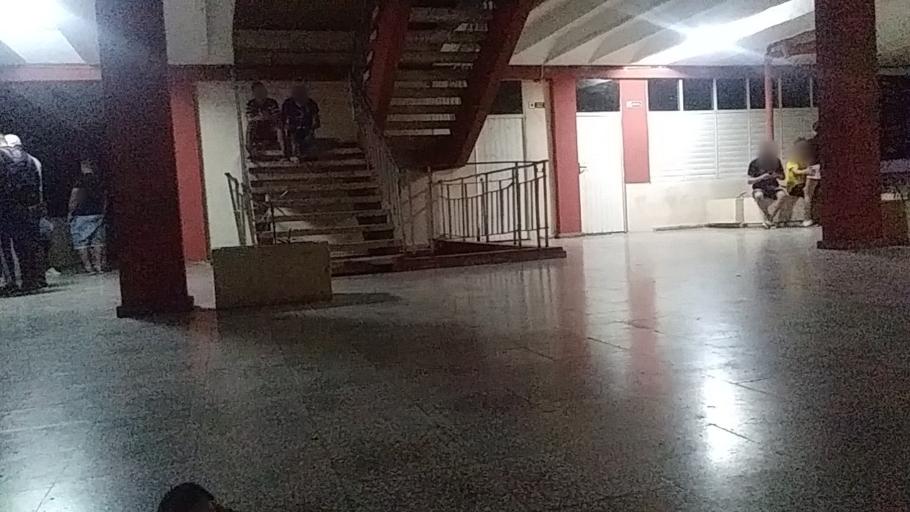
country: CU
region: Las Tunas
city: Las Tunas
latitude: 20.9586
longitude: -76.9408
